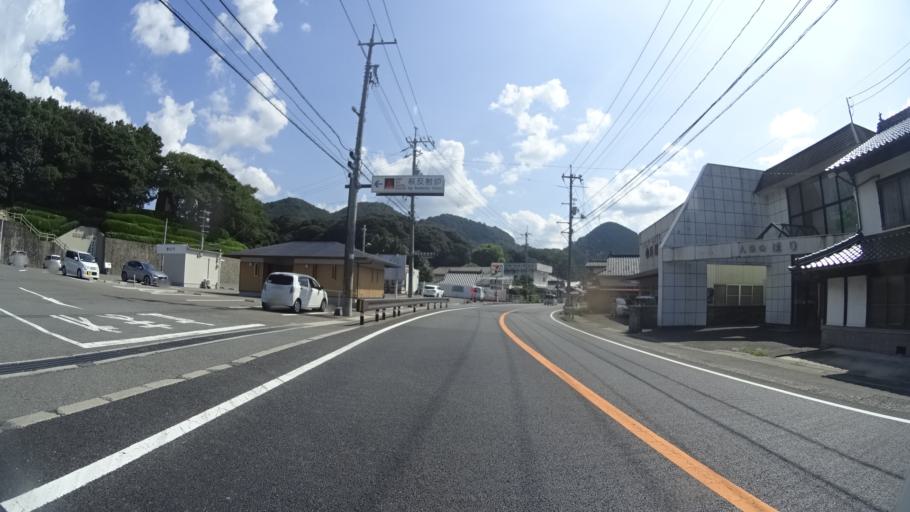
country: JP
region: Yamaguchi
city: Hagi
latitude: 34.4287
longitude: 131.4174
